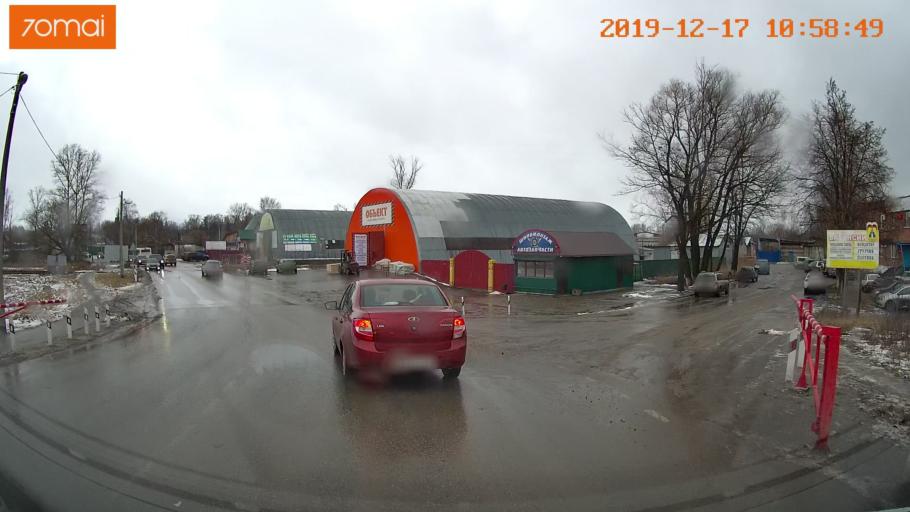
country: RU
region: Vladimir
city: Gus'-Khrustal'nyy
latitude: 55.6227
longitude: 40.6506
